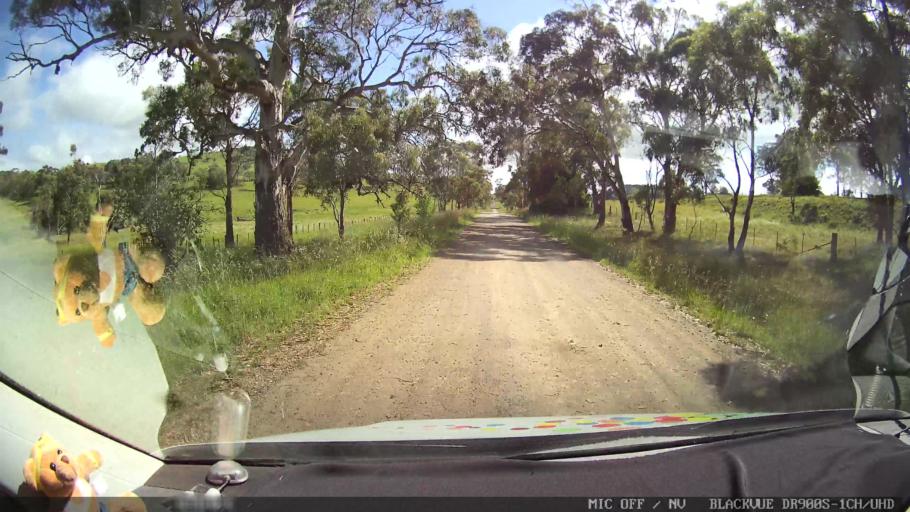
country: AU
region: New South Wales
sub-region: Guyra
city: Guyra
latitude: -30.0114
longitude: 151.6589
